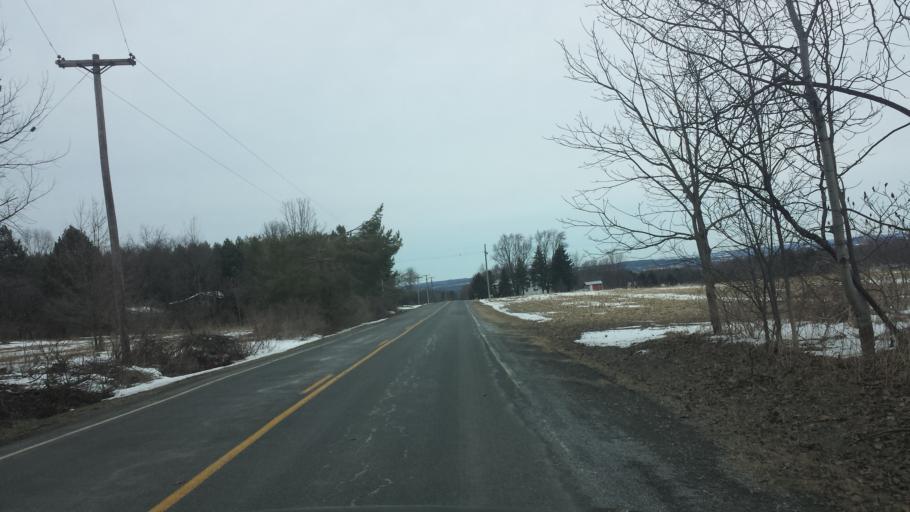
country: US
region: New York
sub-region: Tompkins County
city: Northwest Ithaca
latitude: 42.4913
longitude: -76.5738
